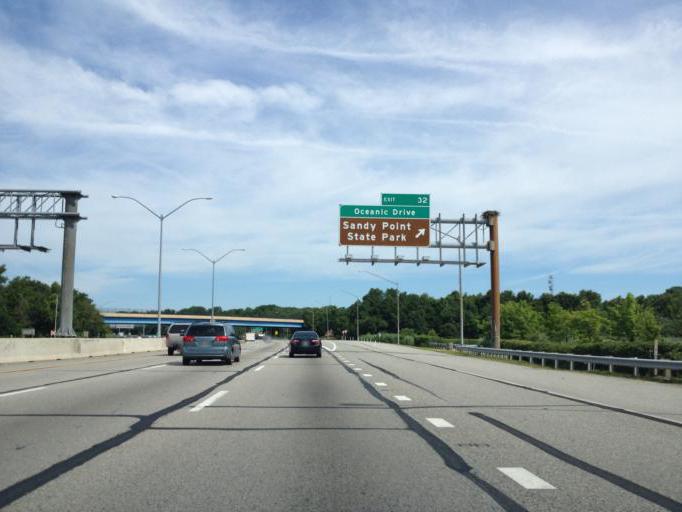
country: US
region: Maryland
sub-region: Anne Arundel County
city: Cape Saint Claire
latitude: 39.0151
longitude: -76.4080
